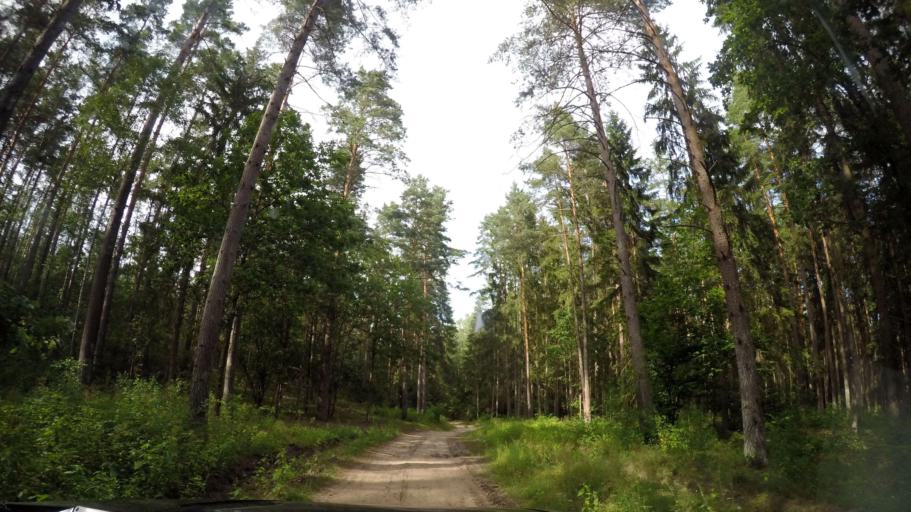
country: BY
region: Grodnenskaya
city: Skidal'
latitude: 53.8354
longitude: 24.1767
